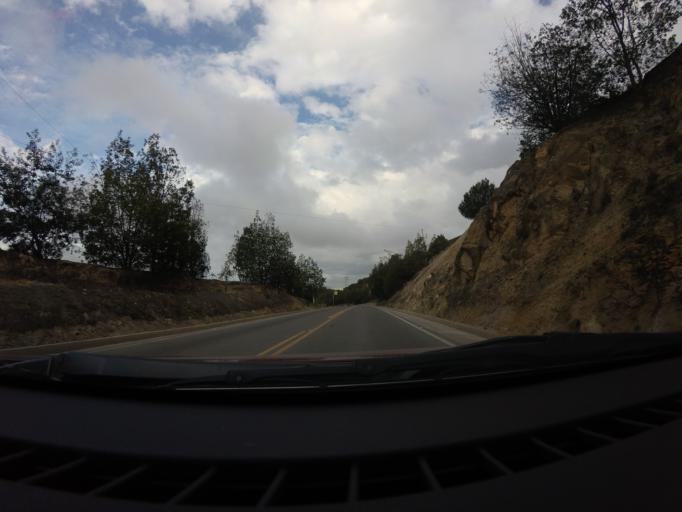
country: CO
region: Boyaca
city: Cucaita
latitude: 5.5647
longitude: -73.4161
